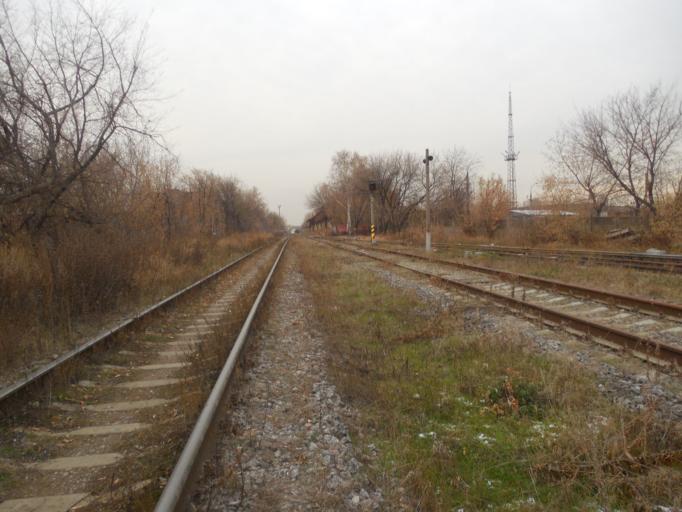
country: RU
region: Moscow
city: Lefortovo
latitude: 55.7397
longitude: 37.7130
